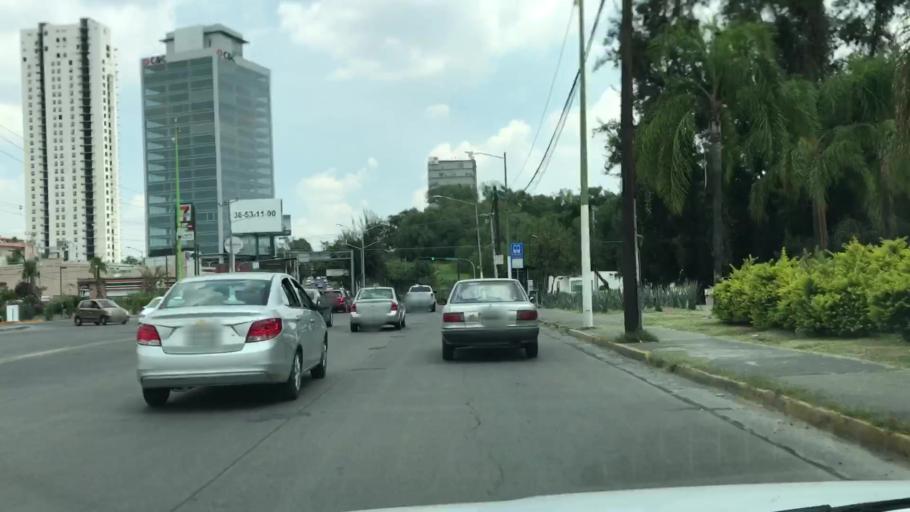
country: MX
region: Jalisco
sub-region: Zapopan
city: Zapopan
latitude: 20.7118
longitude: -103.3809
